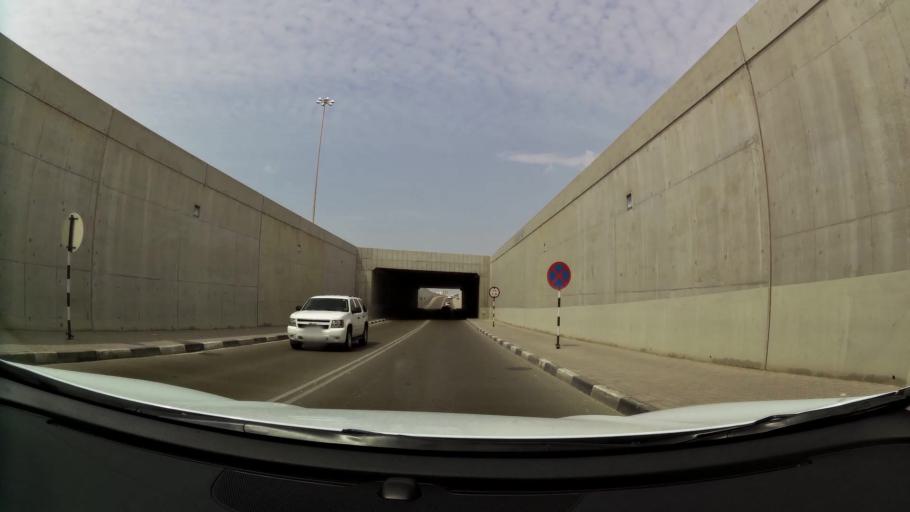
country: AE
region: Abu Dhabi
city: Abu Dhabi
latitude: 24.5373
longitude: 54.6851
